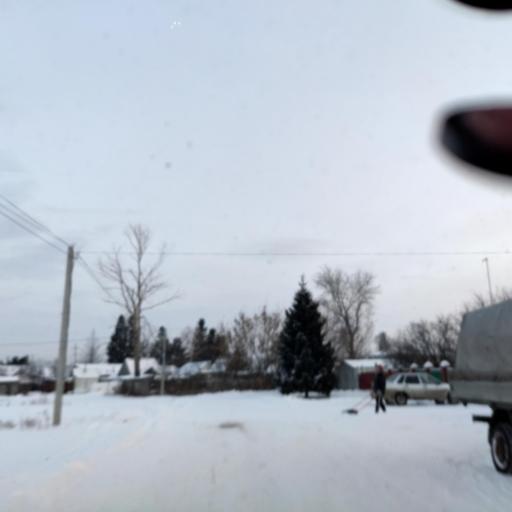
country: RU
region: Bashkortostan
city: Mikhaylovka
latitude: 54.8719
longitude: 55.7332
